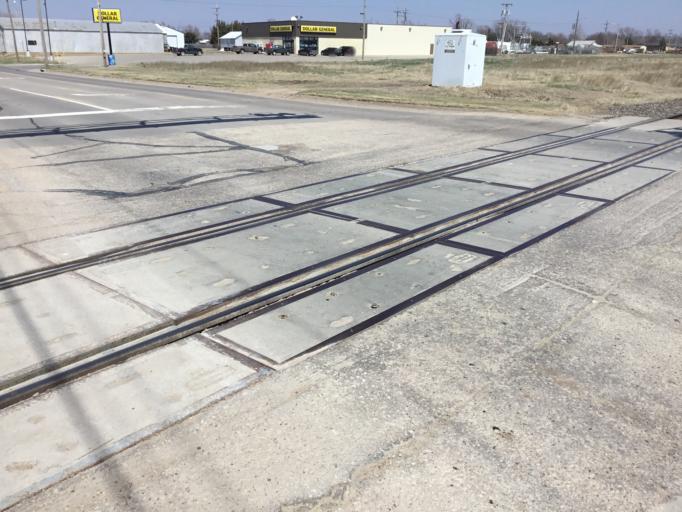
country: US
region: Kansas
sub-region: Russell County
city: Russell
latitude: 38.8952
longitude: -98.8562
